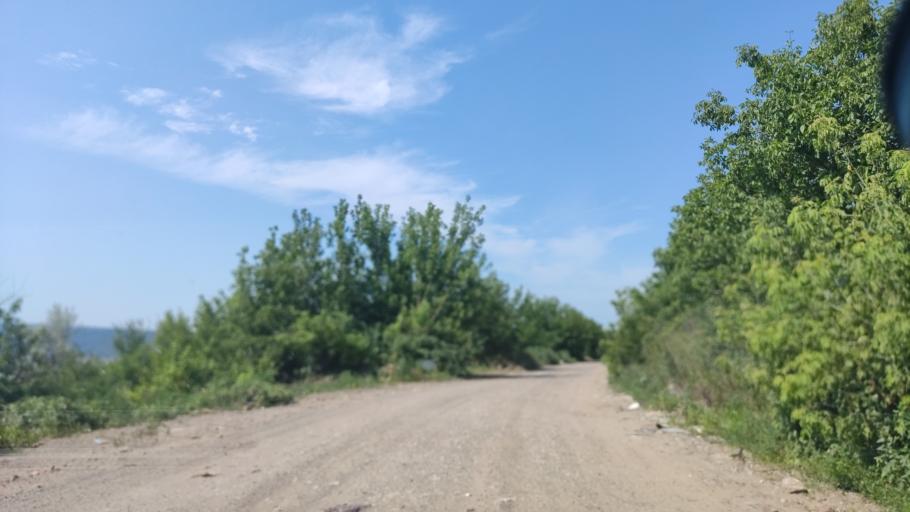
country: MD
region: Raionul Soroca
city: Soroca
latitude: 48.1848
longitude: 28.3133
